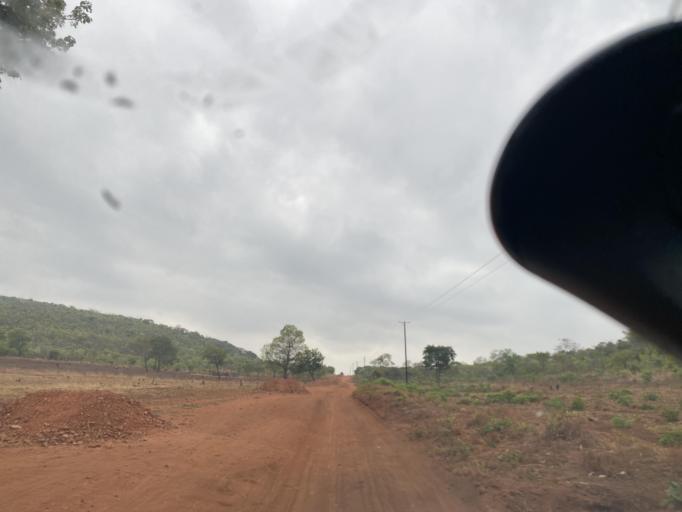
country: ZM
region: Lusaka
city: Chongwe
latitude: -15.1783
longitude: 28.7632
